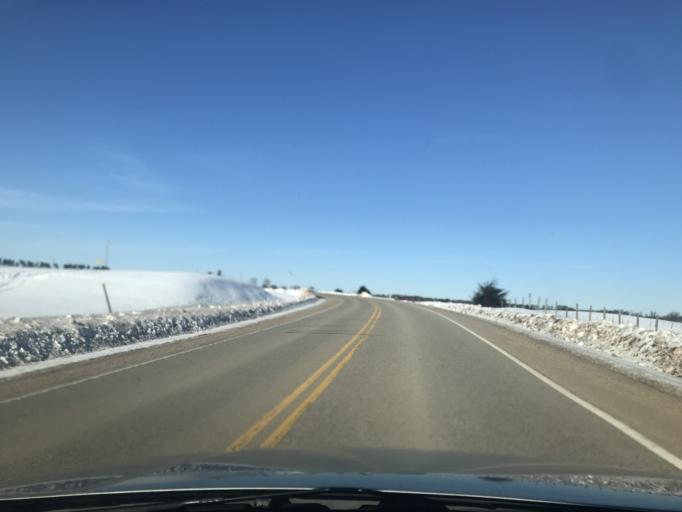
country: US
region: Wisconsin
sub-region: Marinette County
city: Niagara
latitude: 45.4281
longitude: -88.0239
